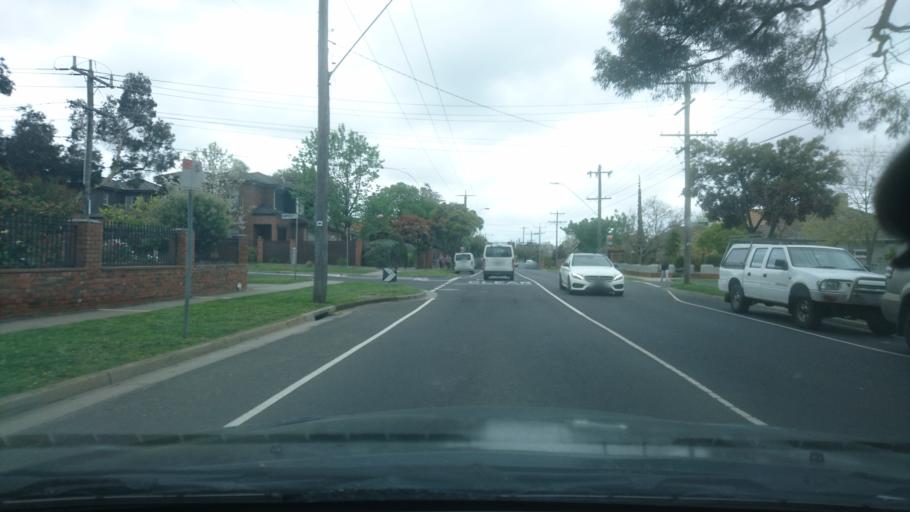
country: AU
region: Victoria
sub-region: Glen Eira
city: Murrumbeena
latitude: -37.8894
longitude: 145.0778
